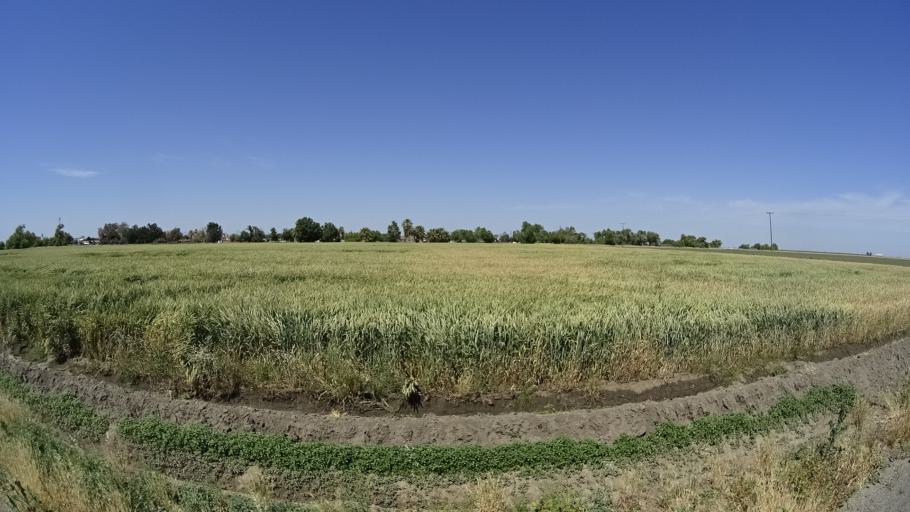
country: US
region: California
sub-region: Kings County
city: Stratford
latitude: 36.1961
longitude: -119.8161
